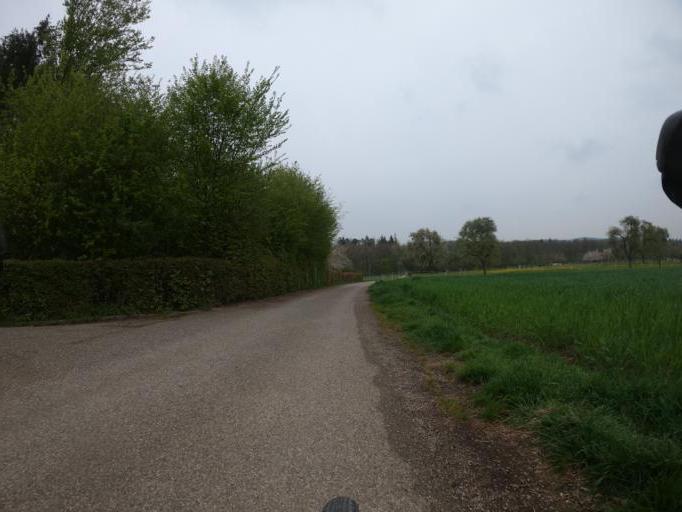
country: DE
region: Baden-Wuerttemberg
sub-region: Karlsruhe Region
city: Illingen
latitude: 48.9644
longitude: 8.9225
